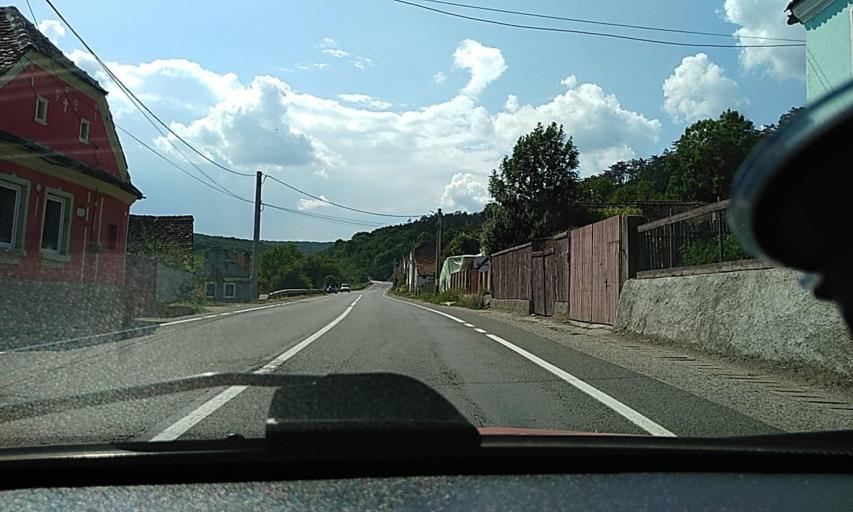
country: RO
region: Brasov
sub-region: Oras Rupea
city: Fiser
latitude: 46.0796
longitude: 25.1401
